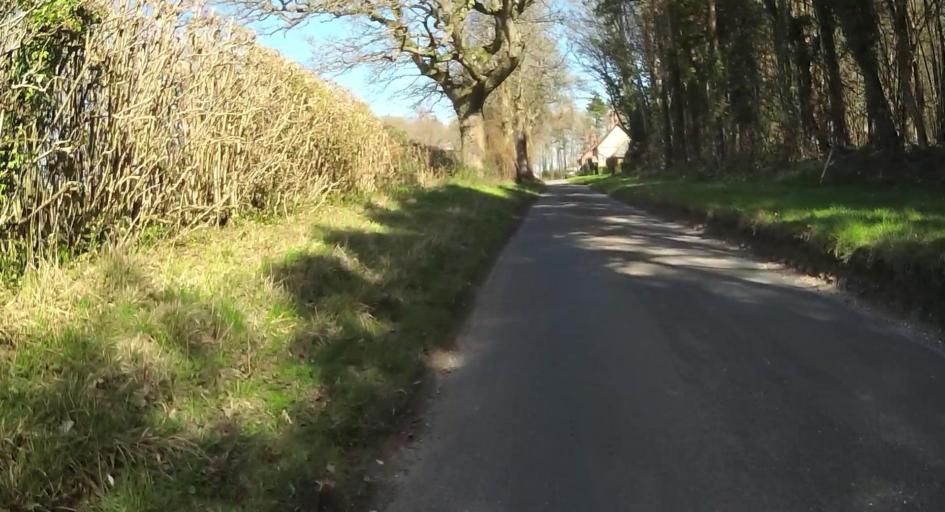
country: GB
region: England
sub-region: Hampshire
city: Overton
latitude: 51.2704
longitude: -1.1940
